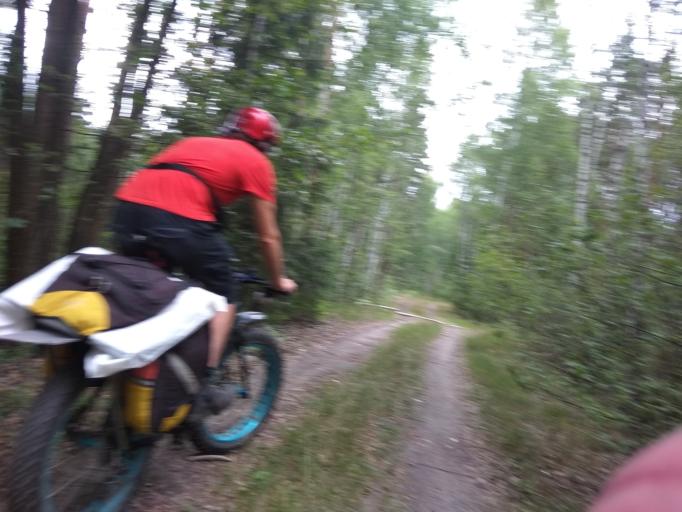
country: RU
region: Moskovskaya
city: Misheronskiy
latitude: 55.6588
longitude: 39.6937
